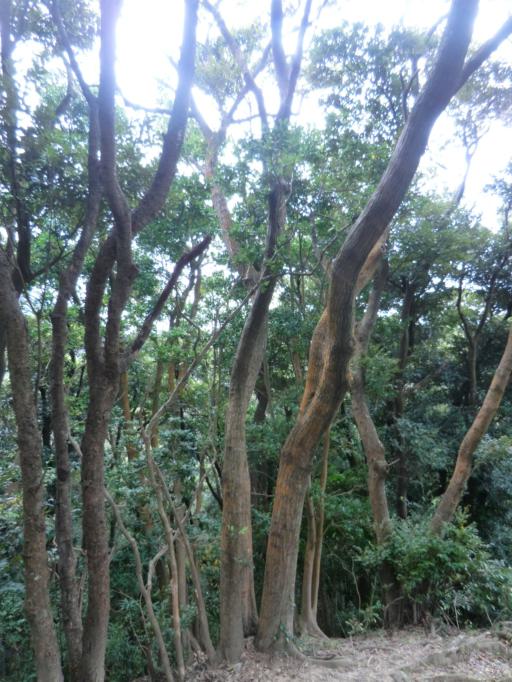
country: JP
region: Chiba
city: Futtsu
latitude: 35.1648
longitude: 139.8292
